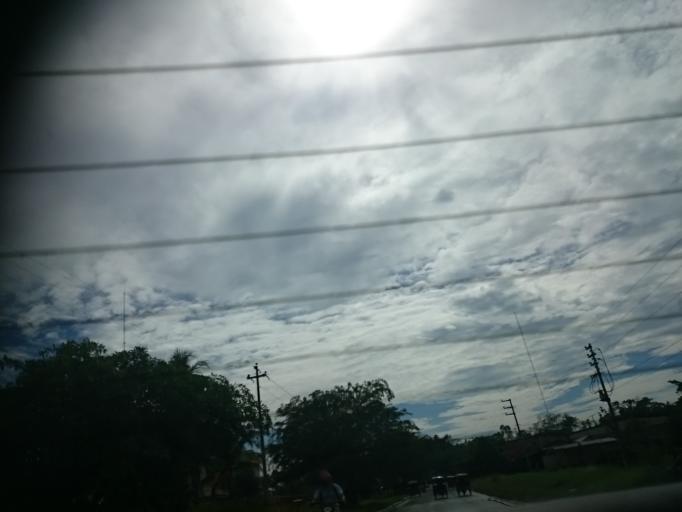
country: PE
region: Loreto
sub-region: Provincia de Maynas
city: Iquitos
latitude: -3.8116
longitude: -73.3177
